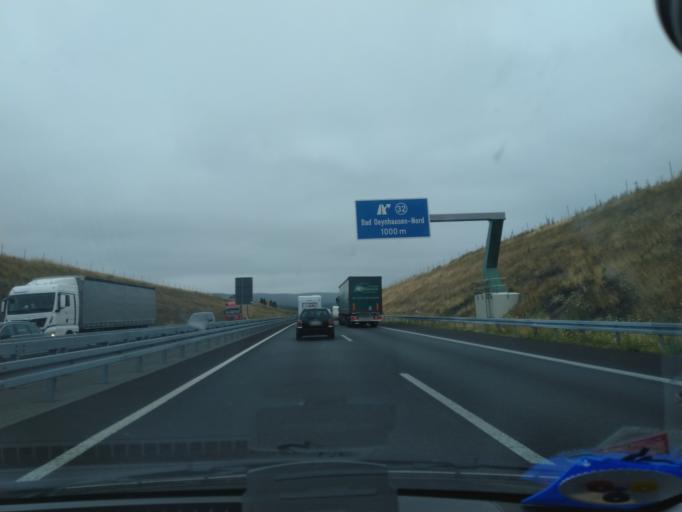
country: DE
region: North Rhine-Westphalia
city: Bad Oeynhausen
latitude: 52.2278
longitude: 8.7754
